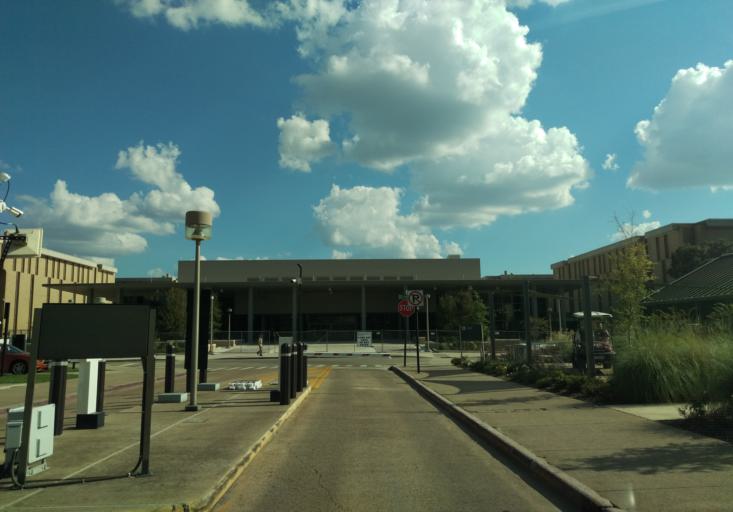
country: US
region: Texas
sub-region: Brazos County
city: College Station
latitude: 30.6161
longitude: -96.3368
